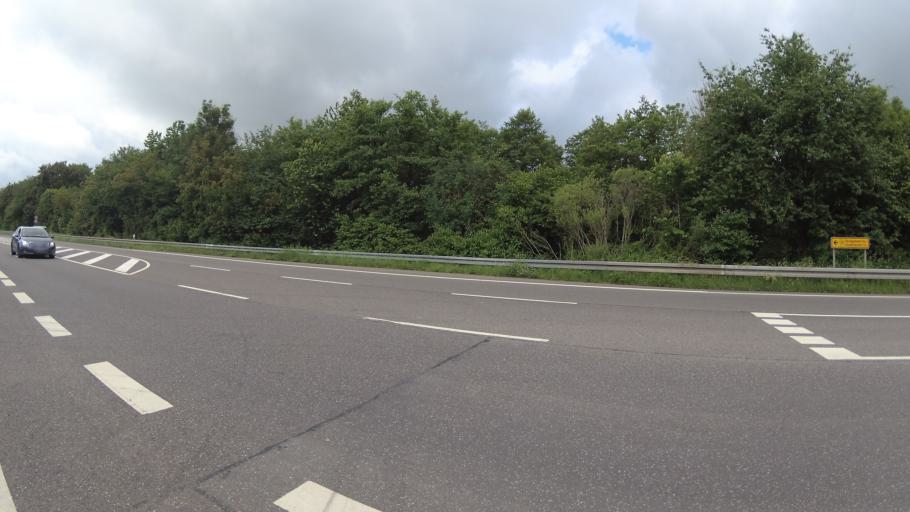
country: FR
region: Lorraine
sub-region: Departement de la Moselle
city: Grosbliederstroff
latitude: 49.1735
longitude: 7.0292
